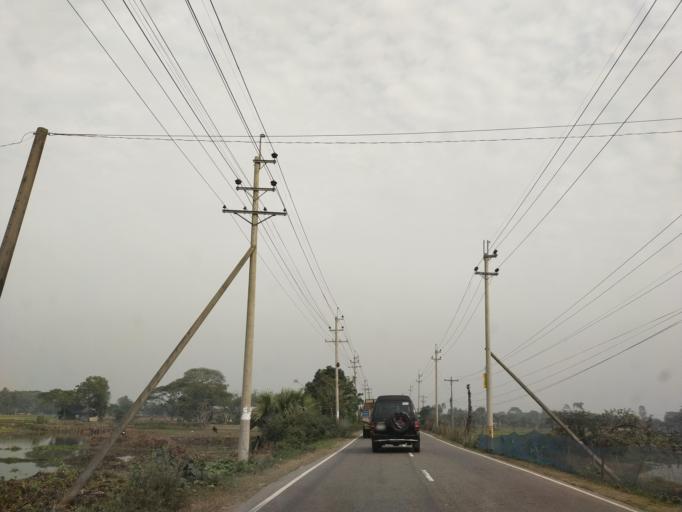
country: BD
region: Dhaka
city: Narsingdi
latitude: 23.9909
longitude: 90.7363
